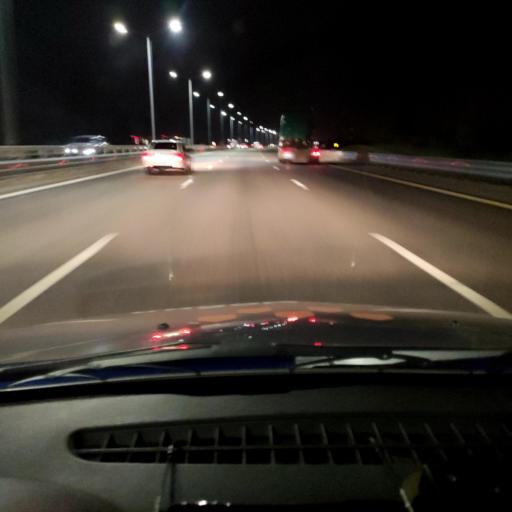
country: RU
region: Voronezj
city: Somovo
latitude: 51.7608
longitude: 39.3068
